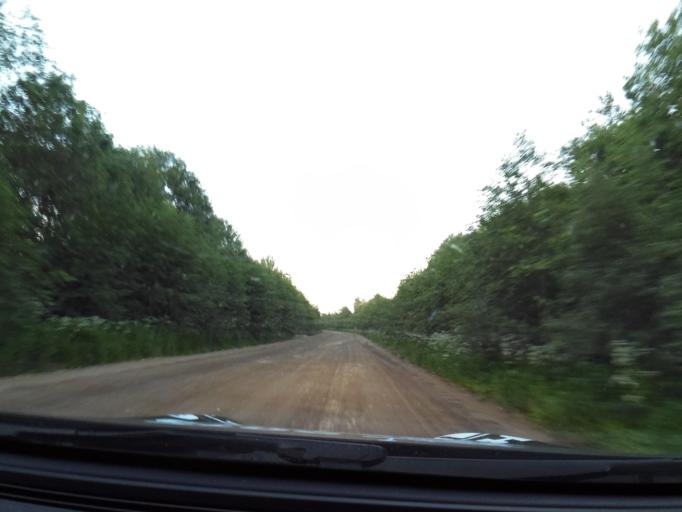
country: RU
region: Leningrad
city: Voznesen'ye
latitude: 60.8388
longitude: 35.7787
